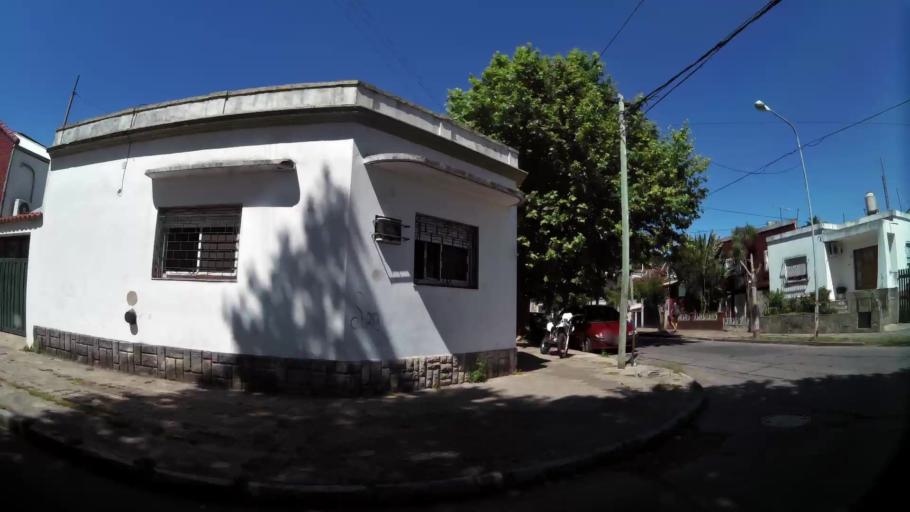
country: AR
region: Buenos Aires
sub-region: Partido de Tigre
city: Tigre
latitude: -34.4299
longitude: -58.5692
